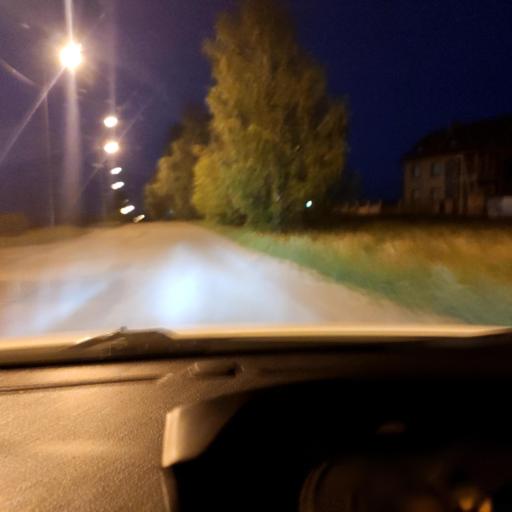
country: RU
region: Tatarstan
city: Vysokaya Gora
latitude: 55.8443
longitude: 49.3316
